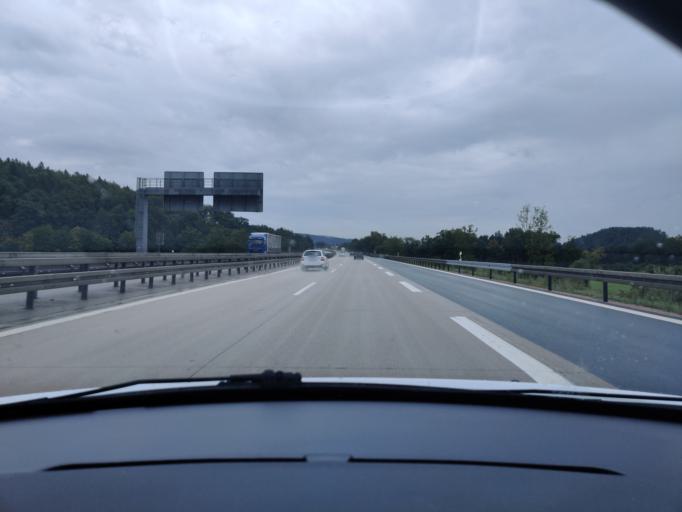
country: DE
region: Bavaria
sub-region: Upper Palatinate
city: Wernberg-Koblitz
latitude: 49.5146
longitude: 12.1683
